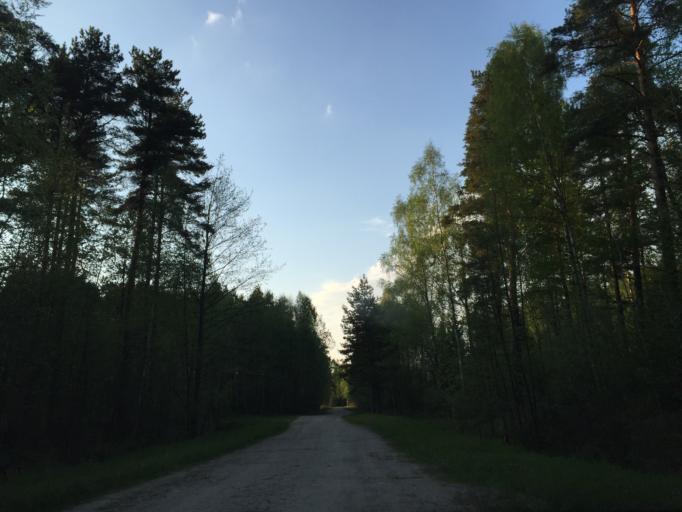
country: LV
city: Tireli
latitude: 56.8892
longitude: 23.6898
